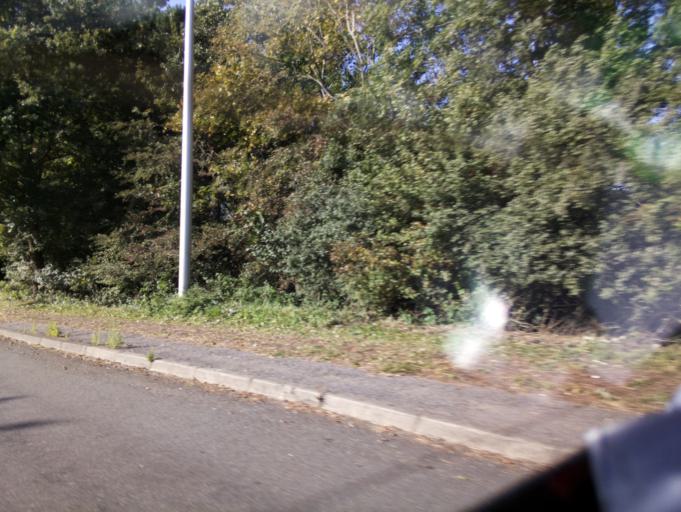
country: GB
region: England
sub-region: West Berkshire
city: Thatcham
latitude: 51.3964
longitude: -1.2035
